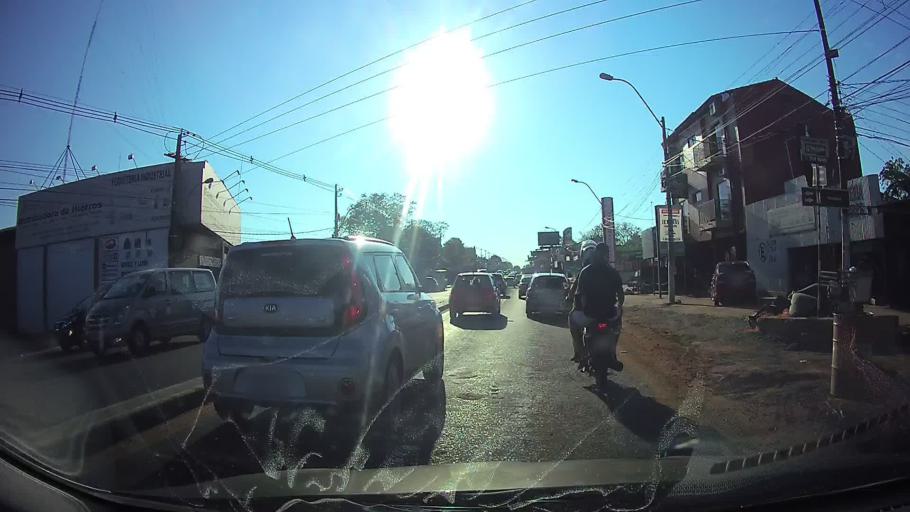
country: PY
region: Central
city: San Lorenzo
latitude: -25.3431
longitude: -57.4906
